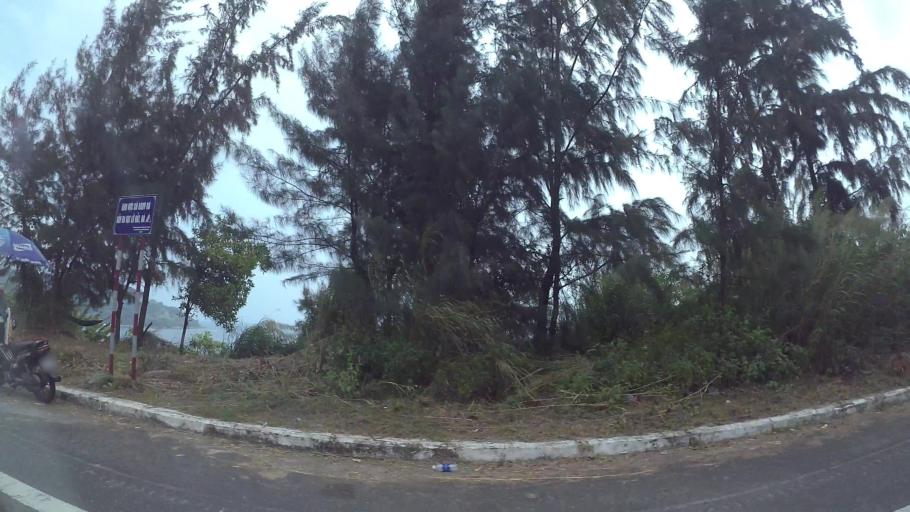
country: VN
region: Da Nang
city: Son Tra
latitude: 16.1054
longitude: 108.2896
